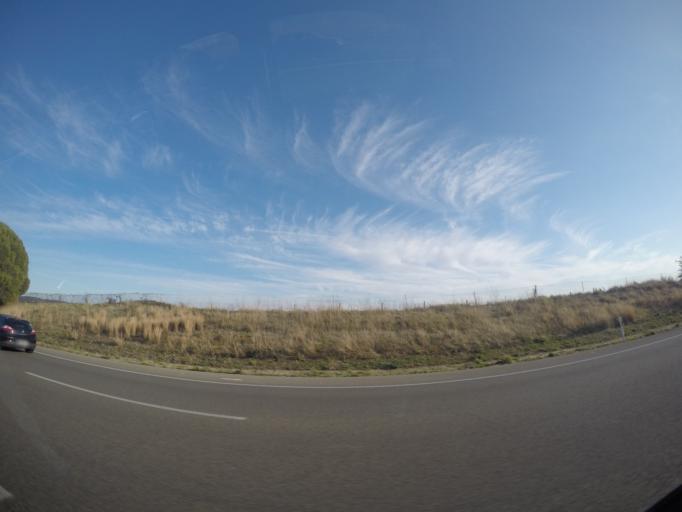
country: ES
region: Catalonia
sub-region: Provincia de Tarragona
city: Sant Jaume dels Domenys
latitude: 41.3036
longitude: 1.6095
